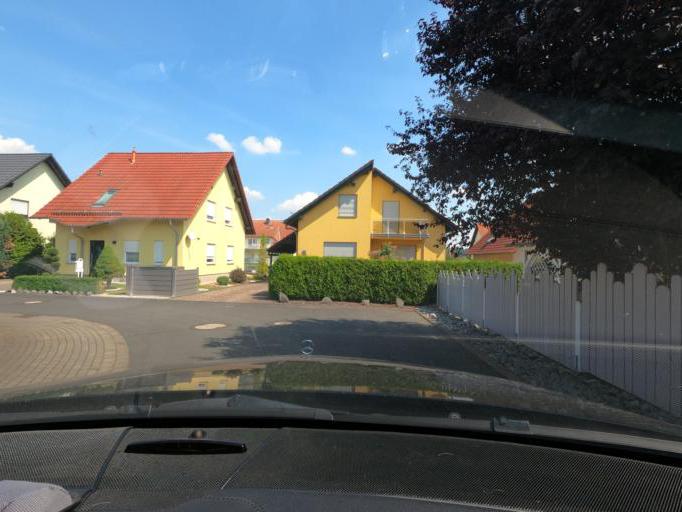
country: DE
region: Thuringia
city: Nordhausen
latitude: 51.5152
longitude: 10.7644
